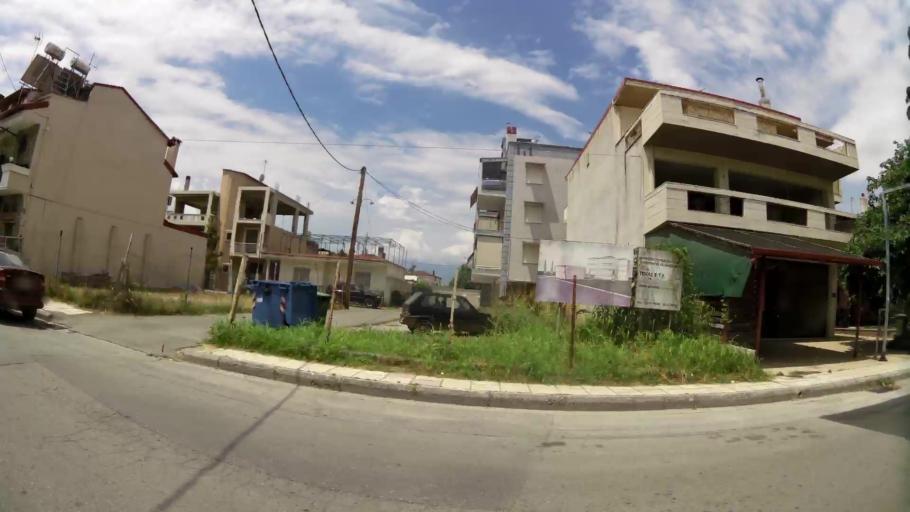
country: GR
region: Central Macedonia
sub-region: Nomos Pierias
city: Katerini
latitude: 40.2623
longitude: 22.5086
